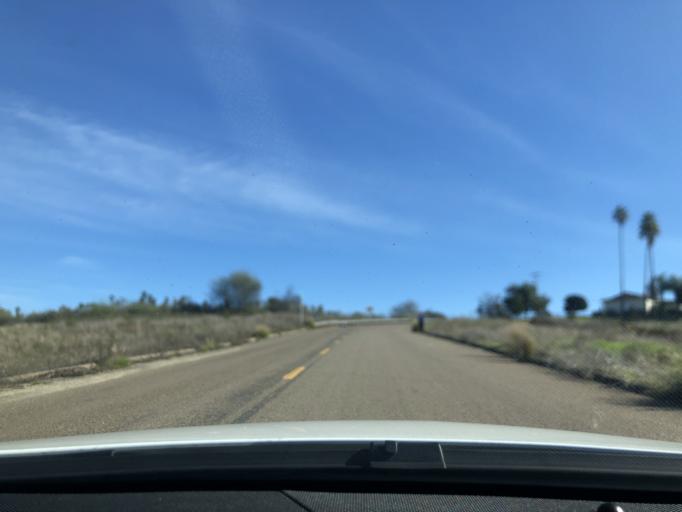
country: US
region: California
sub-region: San Diego County
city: Escondido
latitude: 33.0883
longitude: -117.0800
